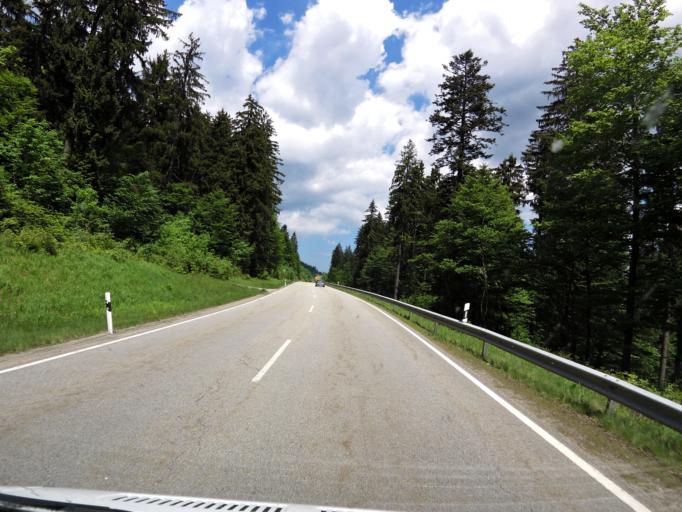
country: DE
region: Bavaria
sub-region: Lower Bavaria
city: Philippsreut
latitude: 48.8579
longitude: 13.6781
